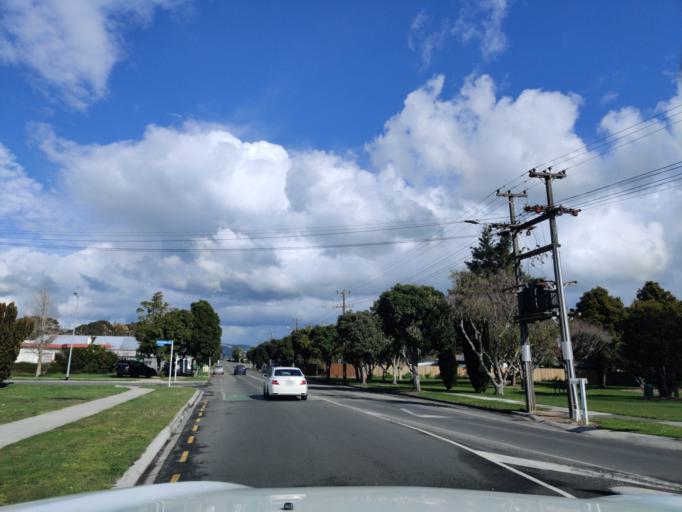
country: NZ
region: Manawatu-Wanganui
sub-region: Palmerston North City
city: Palmerston North
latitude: -40.2930
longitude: 175.7542
